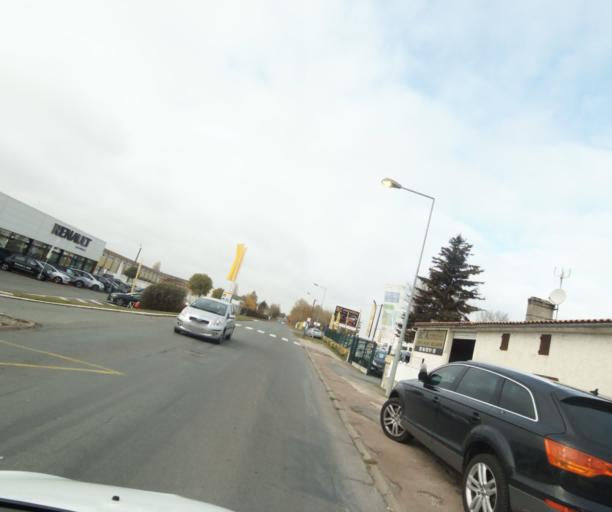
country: FR
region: Poitou-Charentes
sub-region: Departement de la Charente-Maritime
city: Saintes
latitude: 45.7463
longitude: -0.6636
